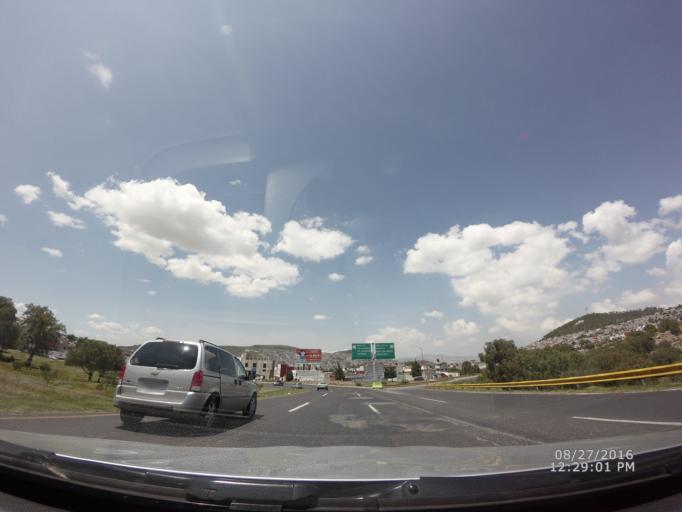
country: MX
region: Hidalgo
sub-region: Mineral de la Reforma
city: Rio de la Soledad
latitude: 20.1190
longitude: -98.7110
